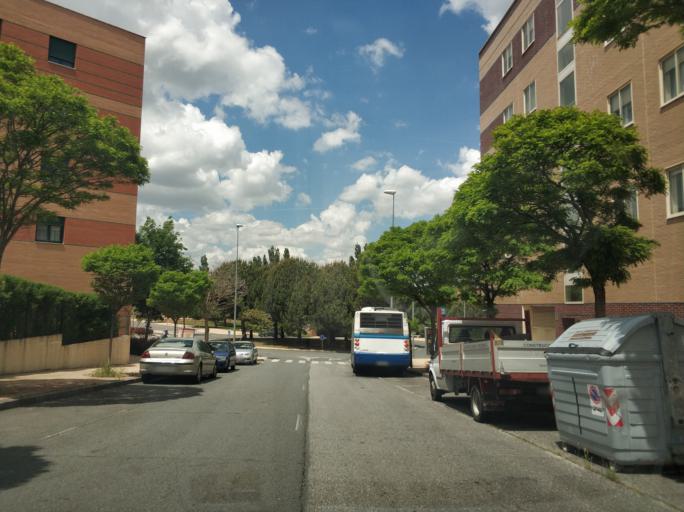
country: ES
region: Castille and Leon
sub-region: Provincia de Salamanca
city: Aldeatejada
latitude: 40.9521
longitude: -5.6898
